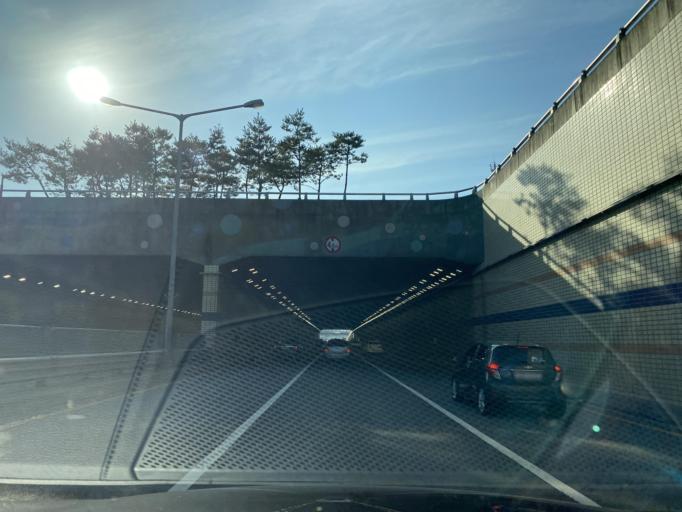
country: KR
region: Chungcheongnam-do
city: Cheonan
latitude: 36.7823
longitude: 127.0936
